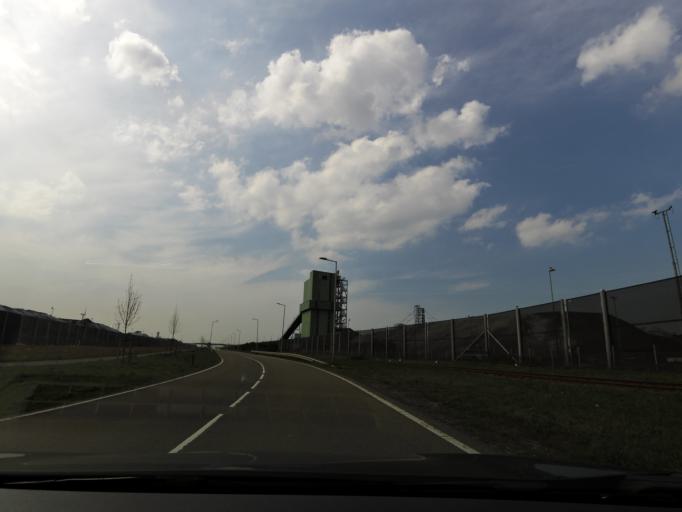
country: NL
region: South Holland
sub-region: Gemeente Rotterdam
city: Hoek van Holland
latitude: 51.9531
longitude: 4.1148
